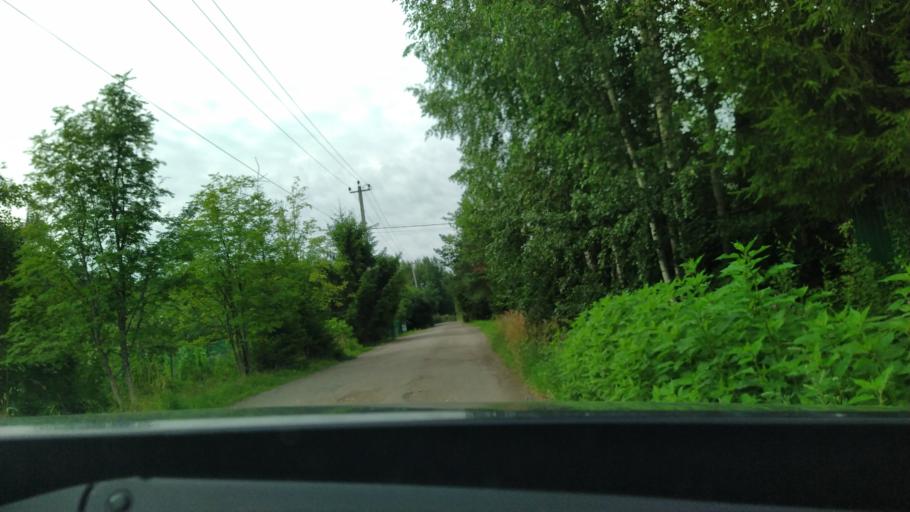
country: RU
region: Leningrad
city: Otradnoye
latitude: 59.7295
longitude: 30.8469
